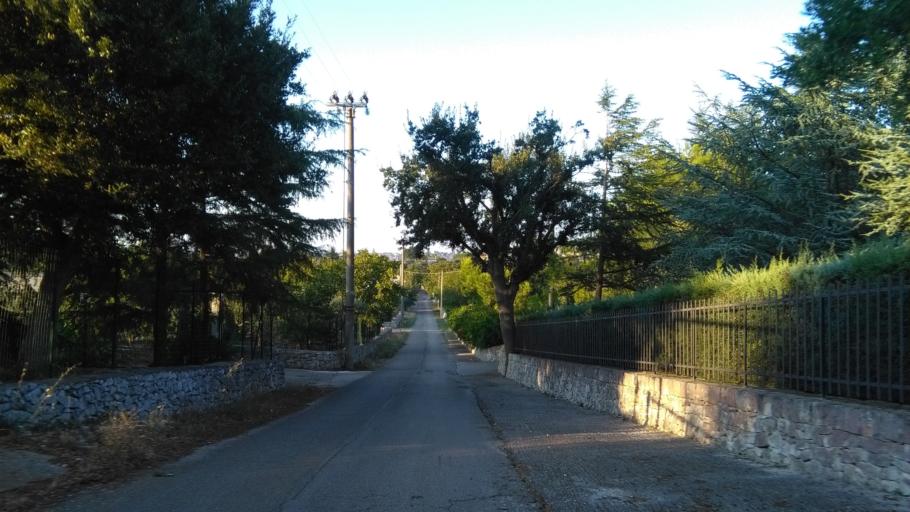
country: IT
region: Apulia
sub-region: Provincia di Bari
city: Putignano
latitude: 40.8244
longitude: 17.0912
